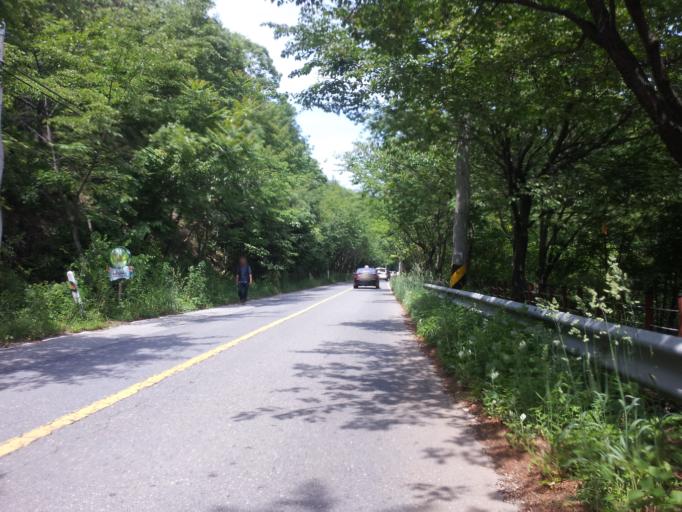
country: KR
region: Daejeon
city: Sintansin
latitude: 36.4341
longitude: 127.4693
